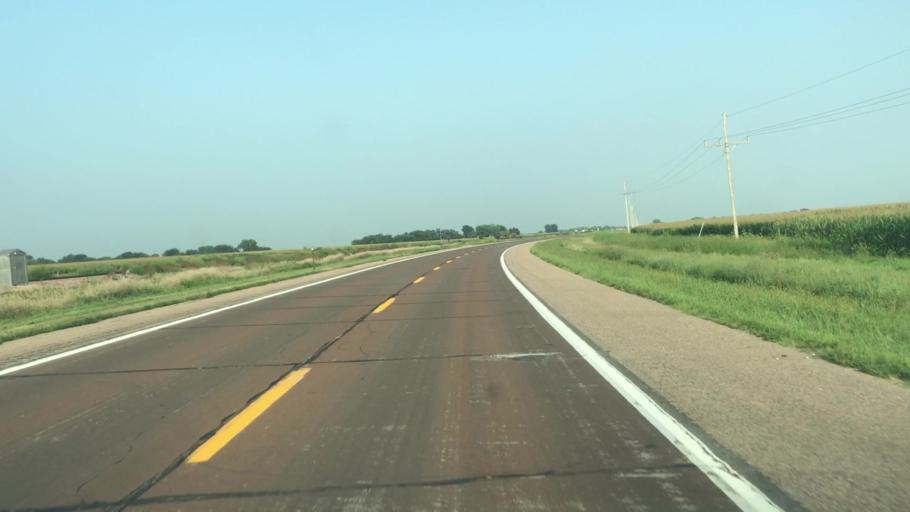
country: US
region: Nebraska
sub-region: Hall County
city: Grand Island
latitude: 40.9672
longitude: -98.4477
